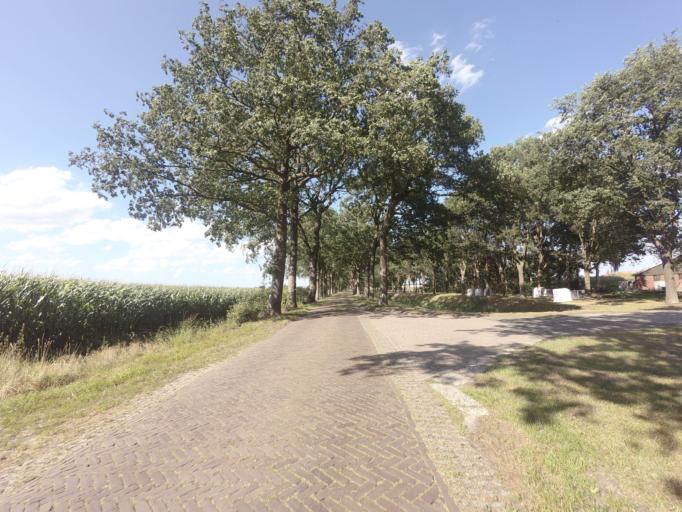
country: NL
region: Drenthe
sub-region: Gemeente Hoogeveen
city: Hoogeveen
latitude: 52.6611
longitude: 6.5148
